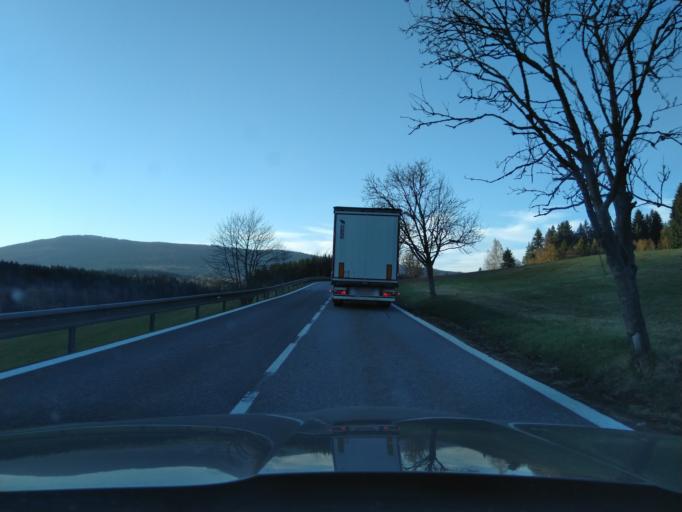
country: CZ
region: Jihocesky
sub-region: Okres Prachatice
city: Vimperk
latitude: 49.0221
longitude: 13.7678
